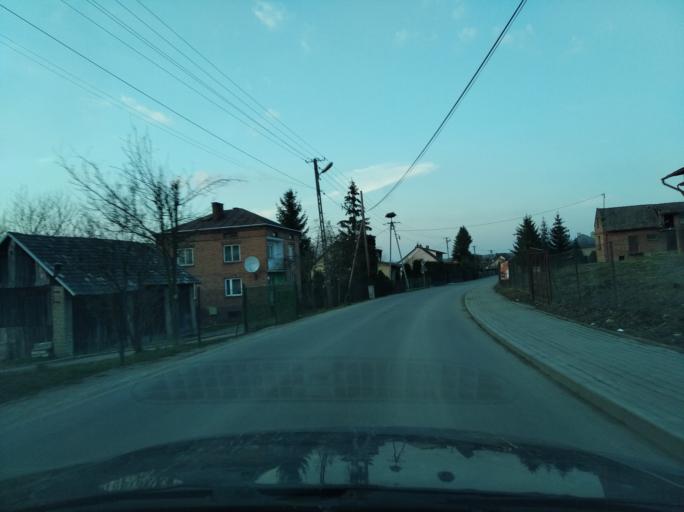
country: PL
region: Subcarpathian Voivodeship
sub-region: Powiat przeworski
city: Zurawiczki
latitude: 50.0202
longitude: 22.5016
